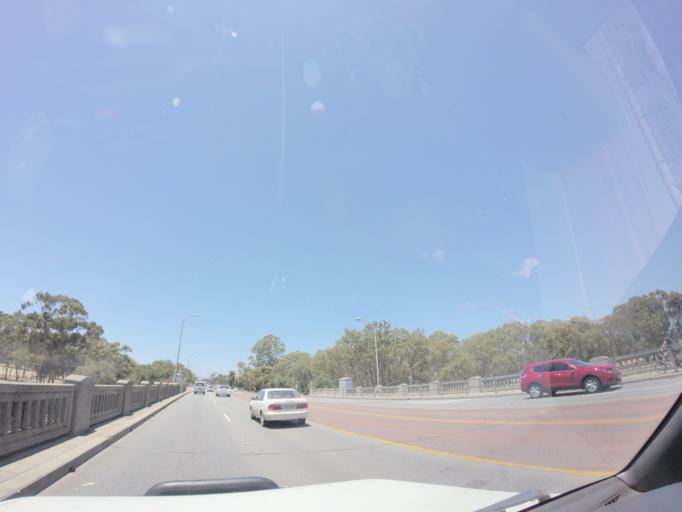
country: AU
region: Western Australia
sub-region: City of Perth
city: East Perth
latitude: -31.9641
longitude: 115.8821
